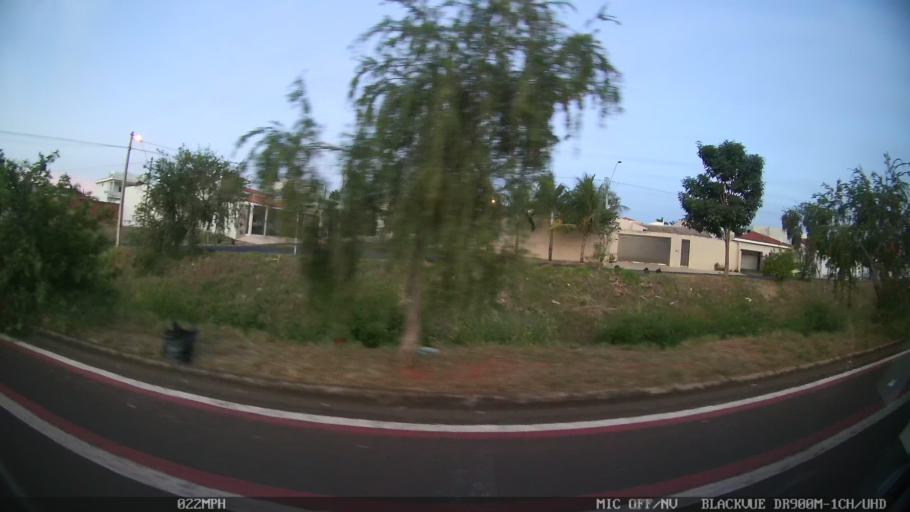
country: BR
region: Sao Paulo
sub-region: Catanduva
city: Catanduva
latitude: -21.1439
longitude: -48.9907
